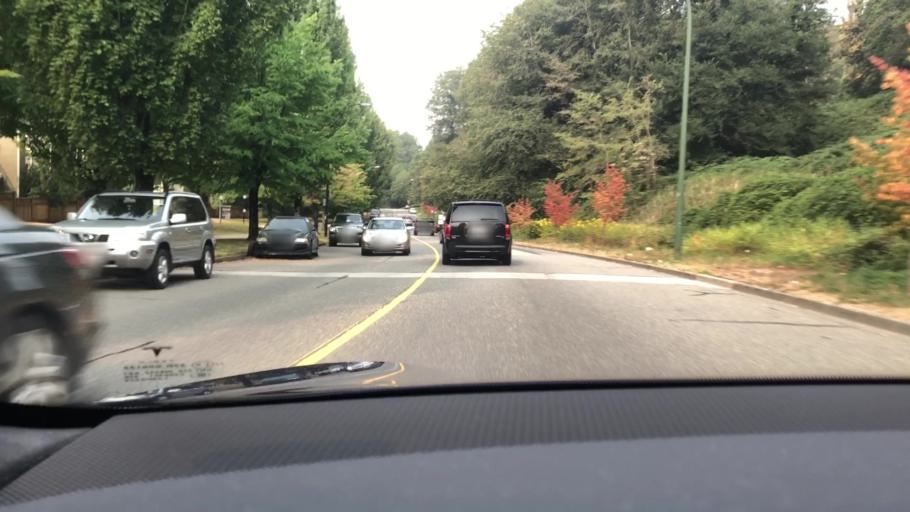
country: CA
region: British Columbia
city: Vancouver
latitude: 49.2084
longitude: -123.0336
